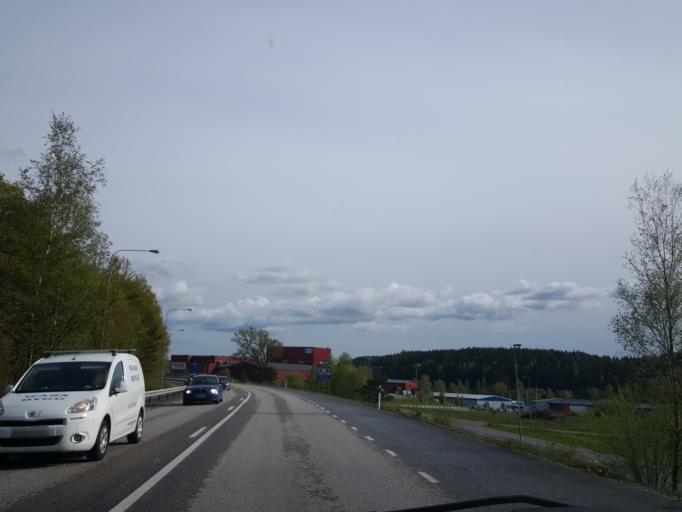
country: SE
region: Vaestra Goetaland
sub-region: Lilla Edets Kommun
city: Lilla Edet
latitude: 58.1119
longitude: 12.1431
